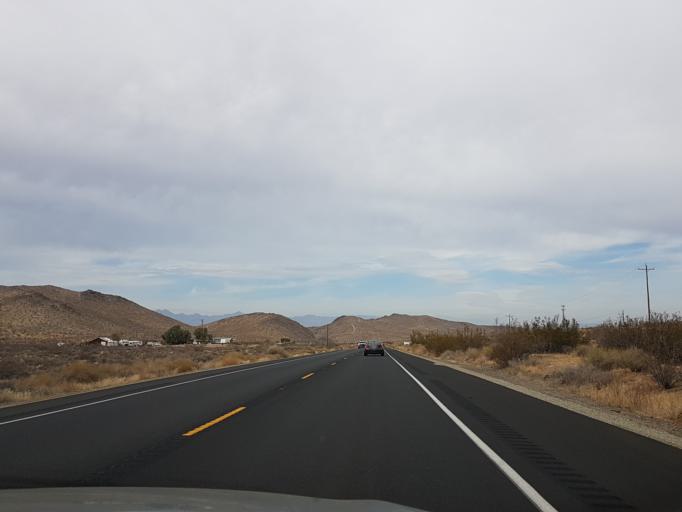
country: US
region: California
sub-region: Kern County
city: Ridgecrest
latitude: 35.5318
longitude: -117.6805
